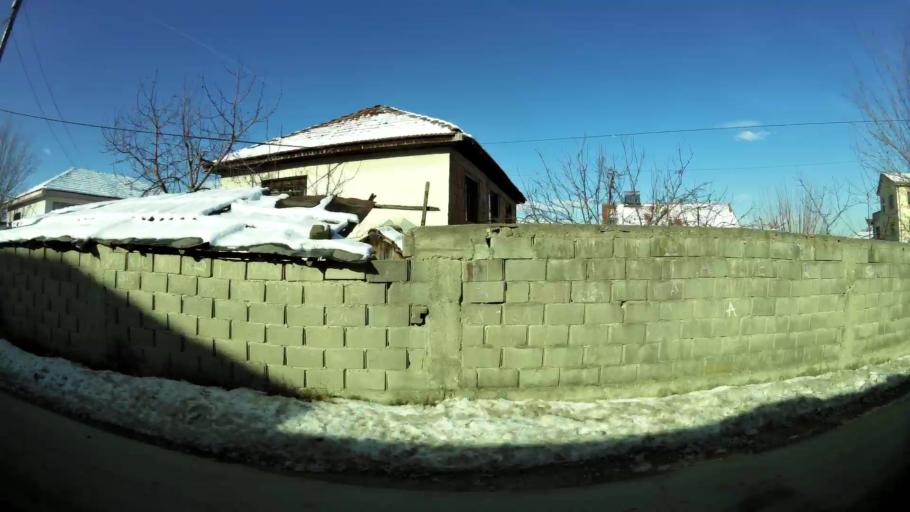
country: MK
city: Grchec
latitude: 41.9941
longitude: 21.3411
